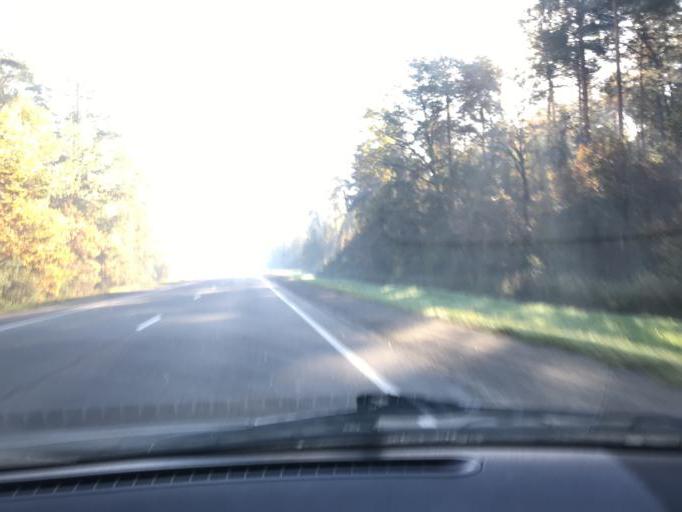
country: BY
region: Brest
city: Horad Luninyets
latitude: 52.2902
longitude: 26.7765
